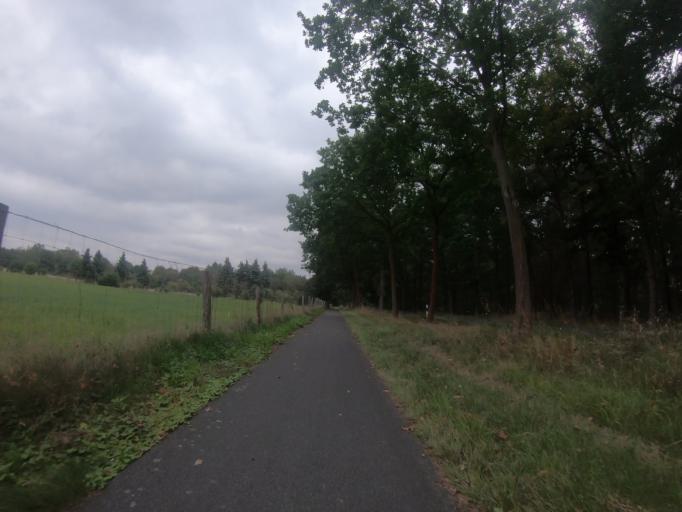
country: DE
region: Lower Saxony
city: Ribbesbuttel
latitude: 52.4466
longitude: 10.5012
